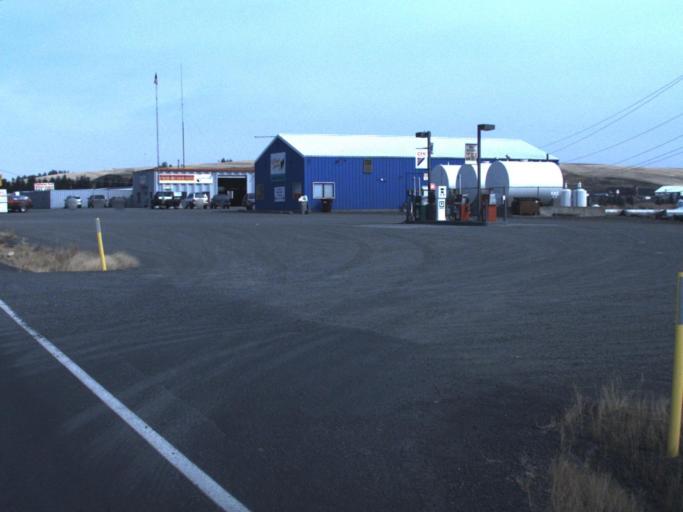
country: US
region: Washington
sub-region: Whitman County
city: Pullman
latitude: 46.7576
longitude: -117.1695
